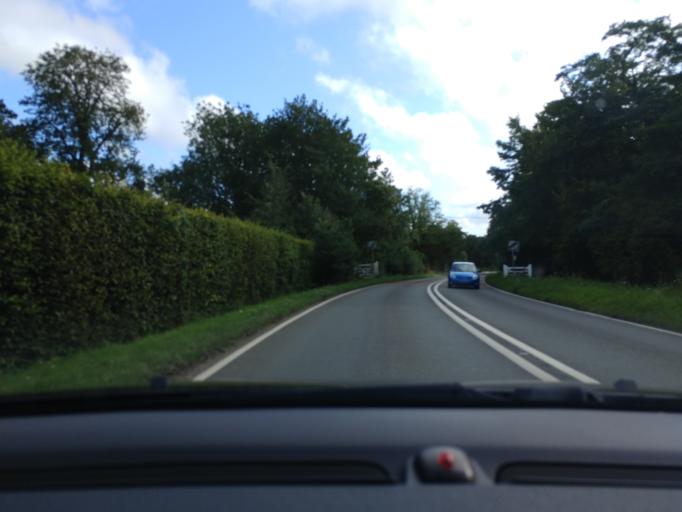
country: GB
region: England
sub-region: Oxfordshire
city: Bicester
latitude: 51.9054
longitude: -1.2239
